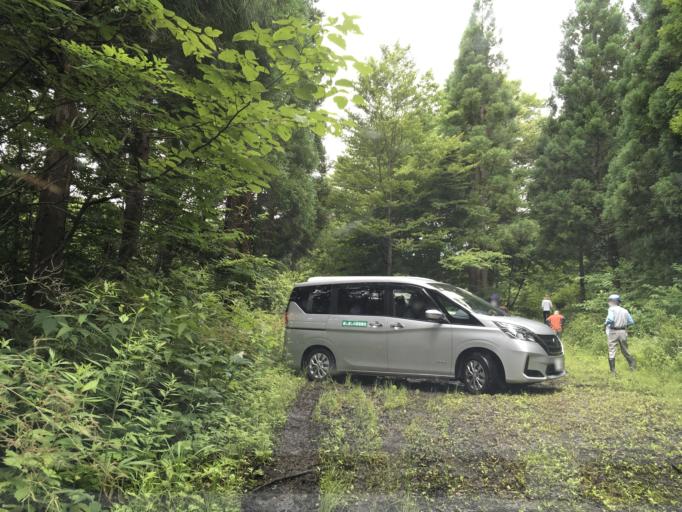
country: JP
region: Iwate
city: Ichinoseki
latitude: 38.9510
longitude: 140.8677
